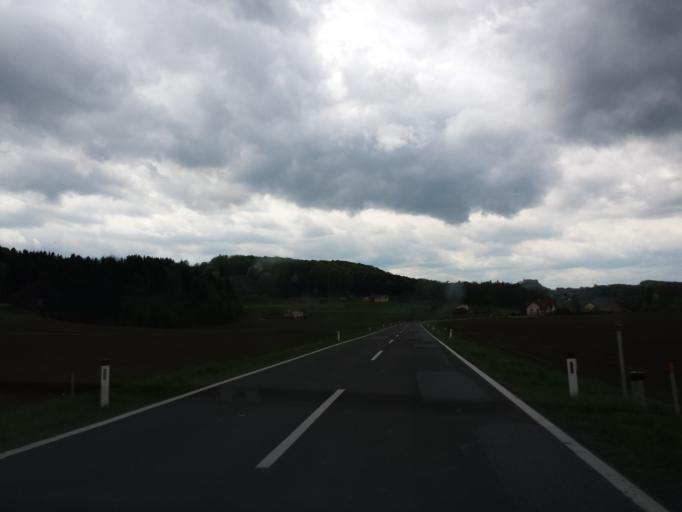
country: AT
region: Styria
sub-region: Politischer Bezirk Suedoststeiermark
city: Hatzendorf
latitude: 46.9871
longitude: 15.9838
